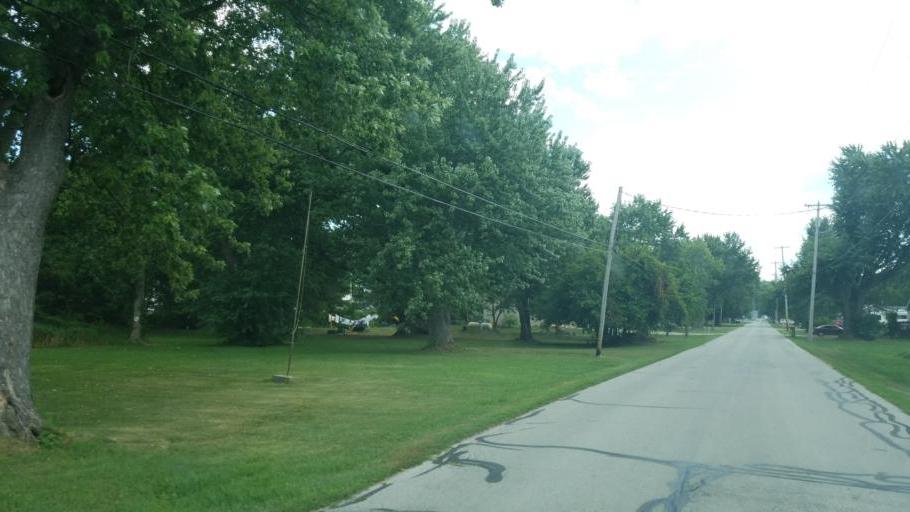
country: US
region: Ohio
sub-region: Lucas County
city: Curtice
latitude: 41.6556
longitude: -83.2493
